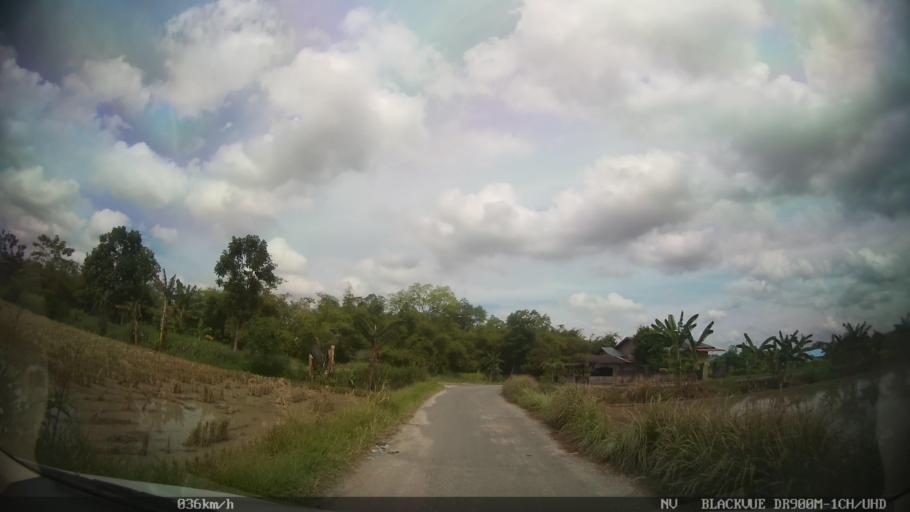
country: ID
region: North Sumatra
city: Percut
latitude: 3.5700
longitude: 98.8511
